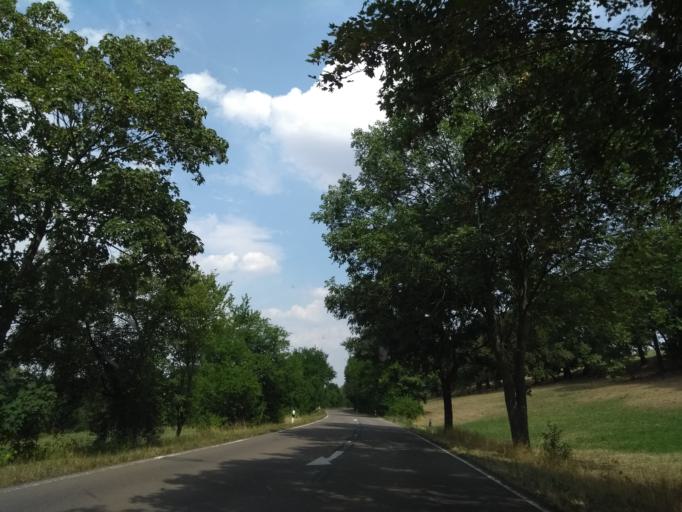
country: DE
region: Saxony-Anhalt
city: Kretzschau
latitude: 51.0281
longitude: 12.0976
